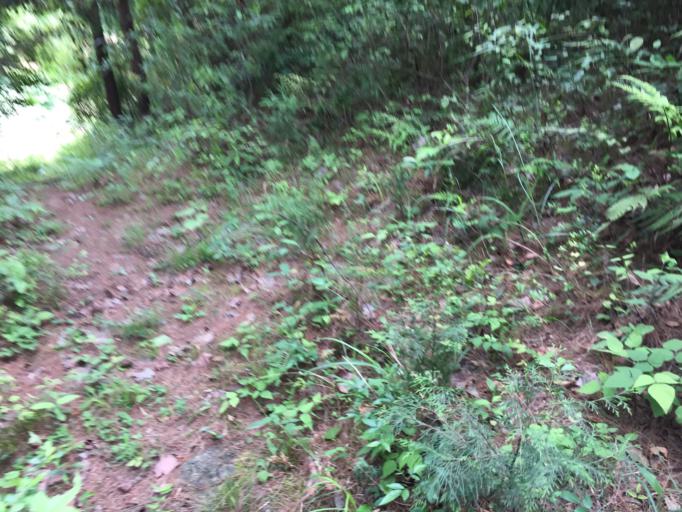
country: CN
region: Guizhou Sheng
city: Shiqian
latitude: 27.6772
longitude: 108.0881
